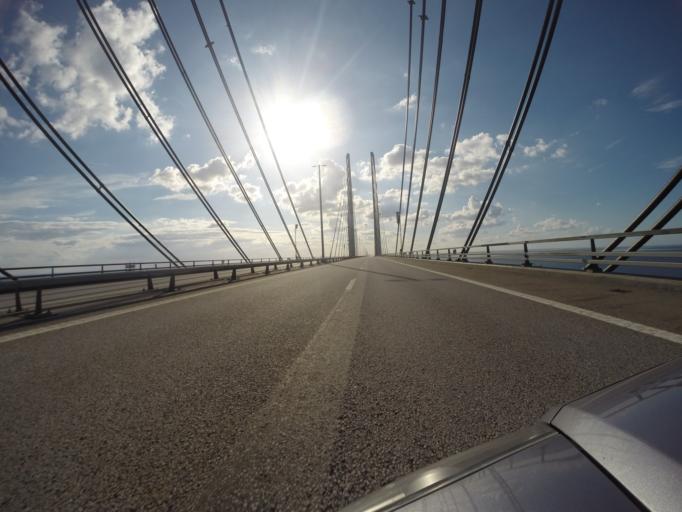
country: SE
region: Skane
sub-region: Malmo
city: Bunkeflostrand
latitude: 55.5749
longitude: 12.8287
